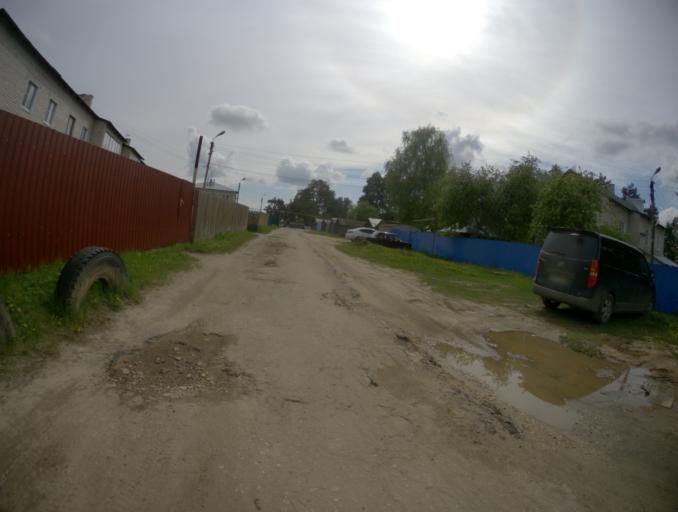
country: RU
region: Rjazan
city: Gus'-Zheleznyy
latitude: 55.0065
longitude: 41.1955
